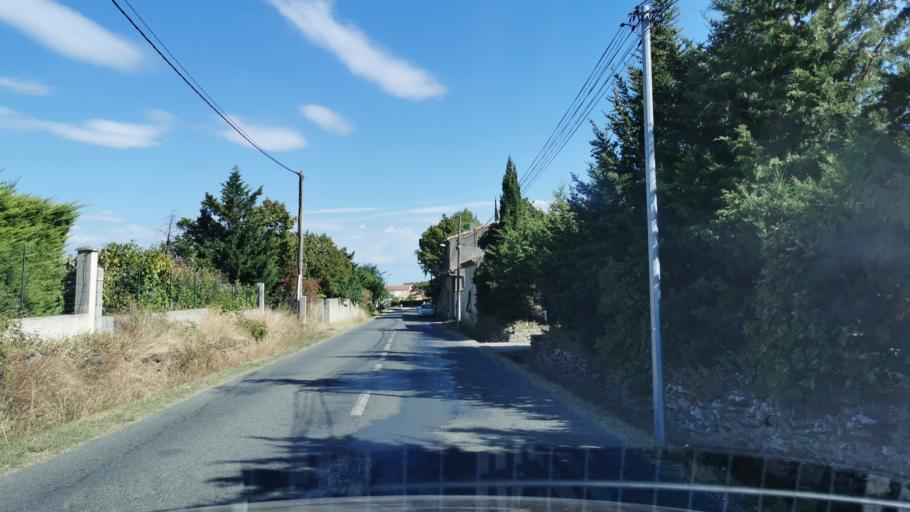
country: FR
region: Languedoc-Roussillon
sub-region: Departement de l'Aude
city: Peyriac-Minervois
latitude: 43.3135
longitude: 2.5550
